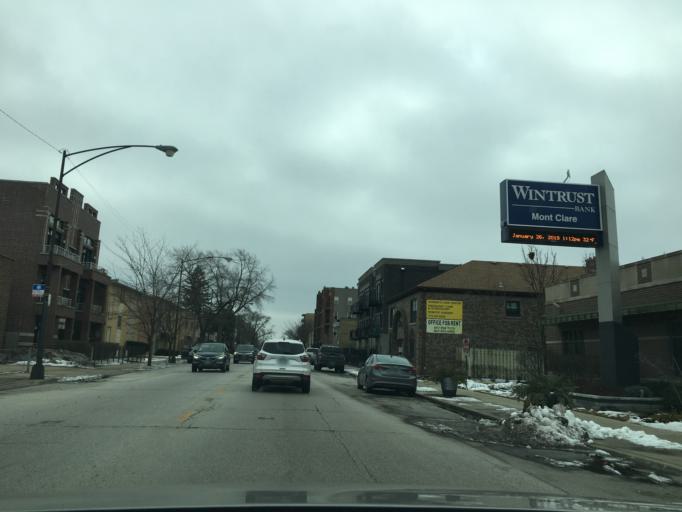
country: US
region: Illinois
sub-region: Cook County
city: Elmwood Park
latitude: 41.9363
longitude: -87.8067
